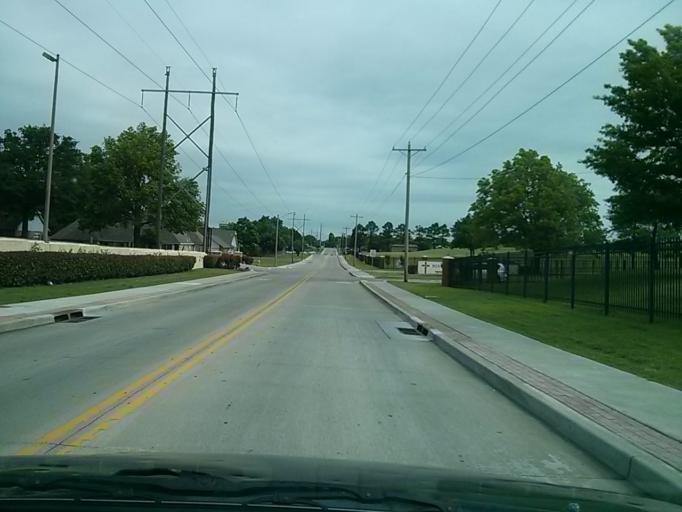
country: US
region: Oklahoma
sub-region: Tulsa County
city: Tulsa
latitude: 36.1059
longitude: -95.9132
